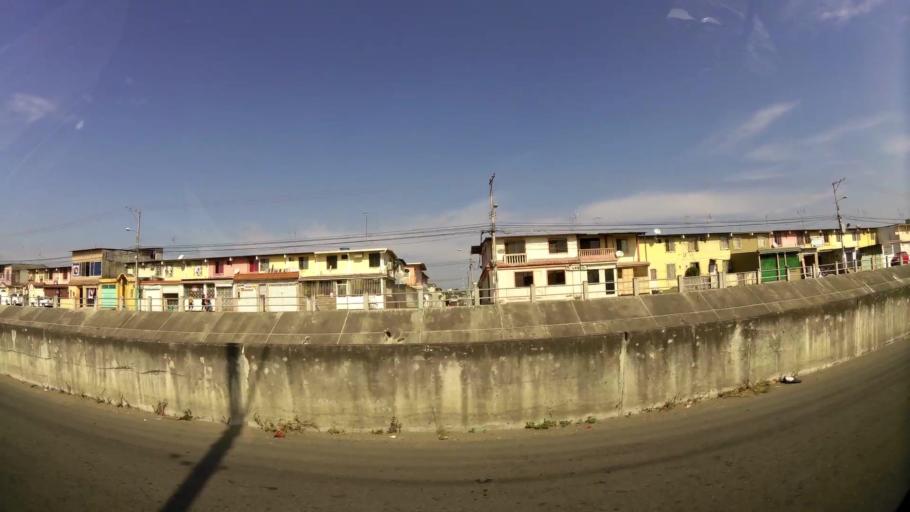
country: EC
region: Guayas
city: Eloy Alfaro
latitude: -2.0910
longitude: -79.9181
